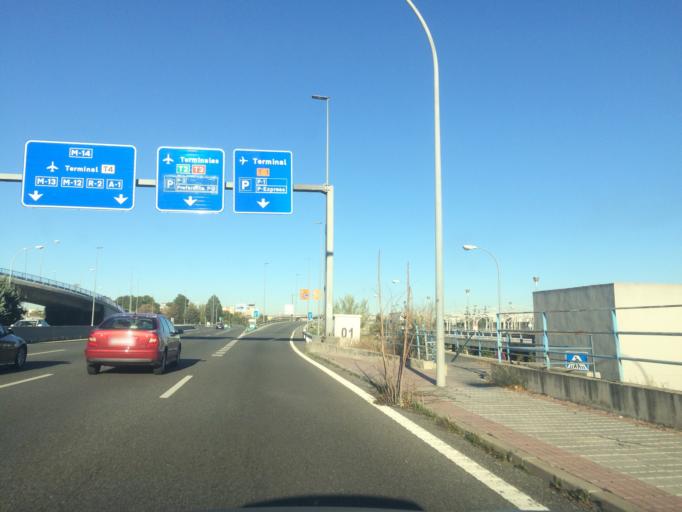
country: ES
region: Madrid
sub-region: Provincia de Madrid
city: Barajas de Madrid
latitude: 40.4614
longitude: -3.5768
